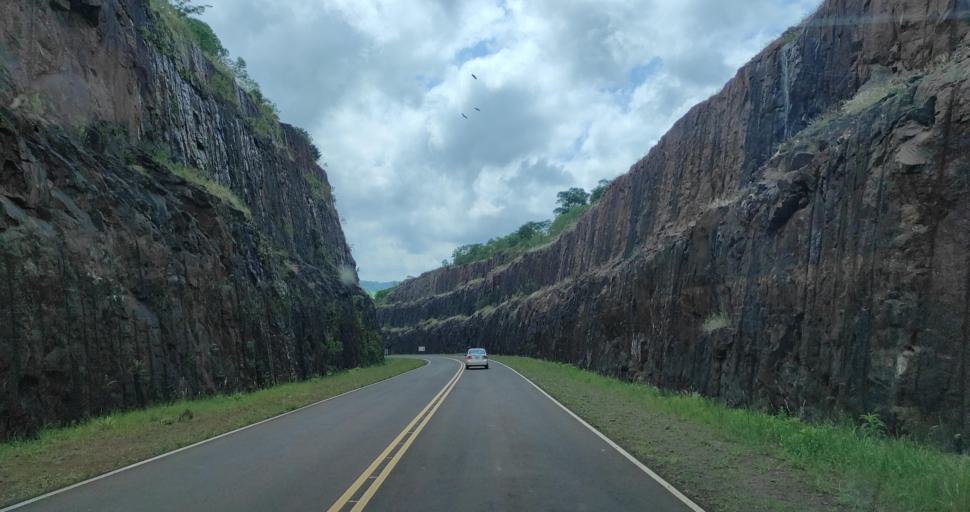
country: AR
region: Misiones
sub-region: Departamento de Veinticinco de Mayo
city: Veinticinco de Mayo
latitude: -27.3769
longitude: -54.8391
